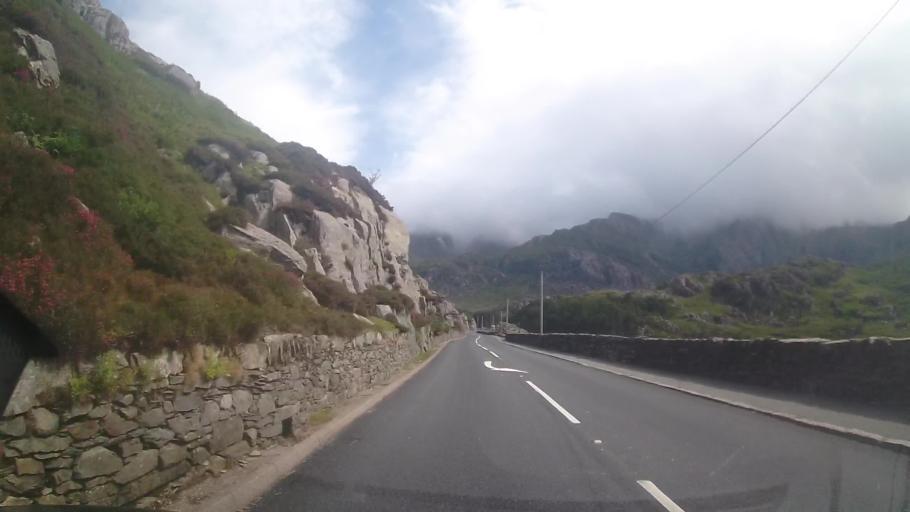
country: GB
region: Wales
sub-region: Gwynedd
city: Bethesda
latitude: 53.1279
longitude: -4.0223
